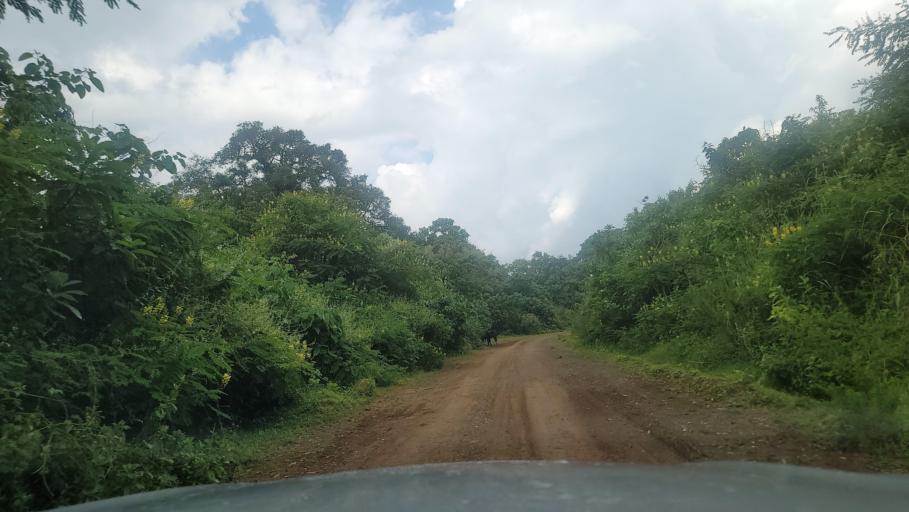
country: ET
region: Southern Nations, Nationalities, and People's Region
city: Bonga
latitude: 7.6359
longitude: 36.2243
